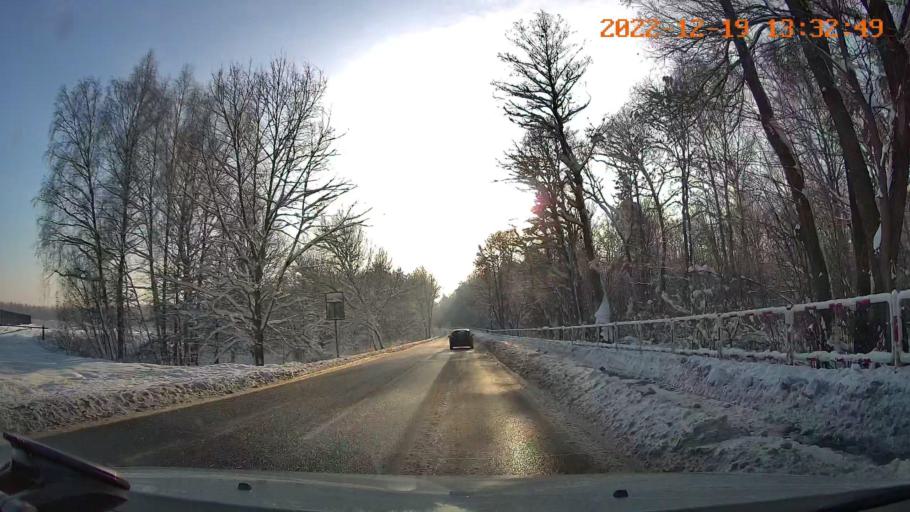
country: PL
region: Silesian Voivodeship
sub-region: Powiat bierunsko-ledzinski
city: Bierun
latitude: 50.1088
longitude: 19.0990
